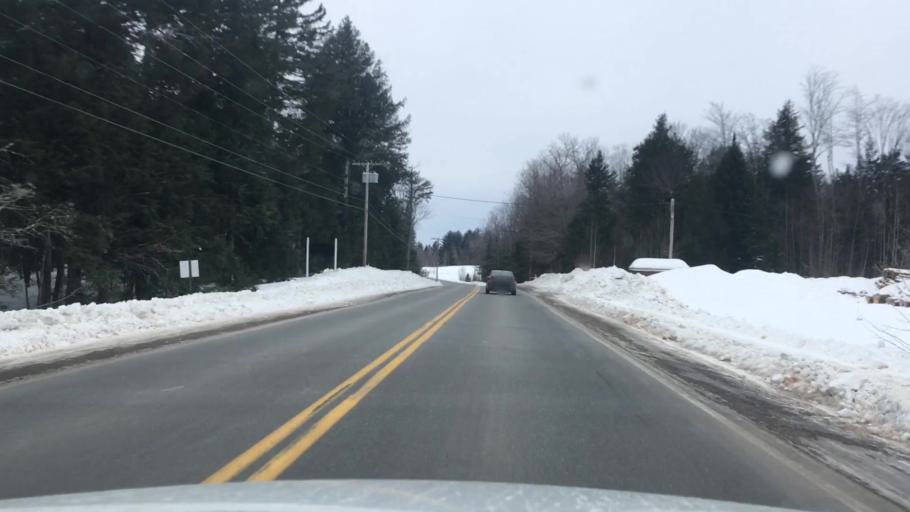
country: US
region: Maine
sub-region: Penobscot County
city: Garland
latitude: 44.9937
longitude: -69.0783
